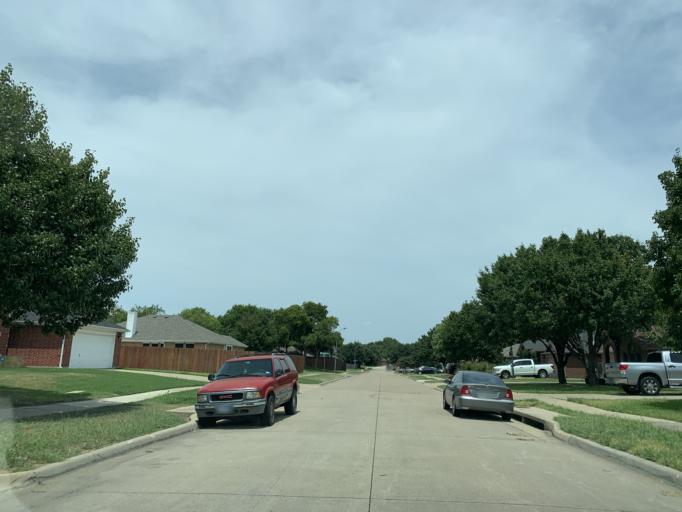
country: US
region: Texas
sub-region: Dallas County
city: Grand Prairie
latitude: 32.6603
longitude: -97.0245
